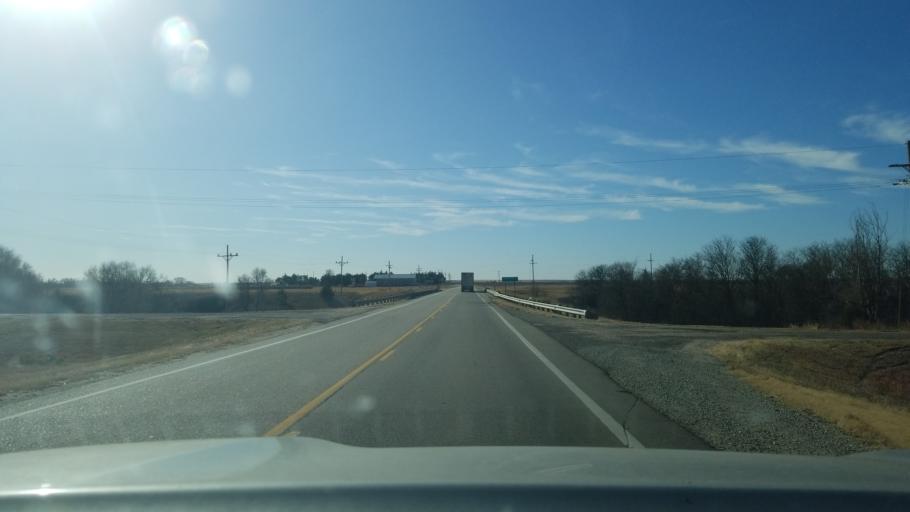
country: US
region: Kansas
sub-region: Ness County
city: Ness City
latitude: 38.4407
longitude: -99.9049
